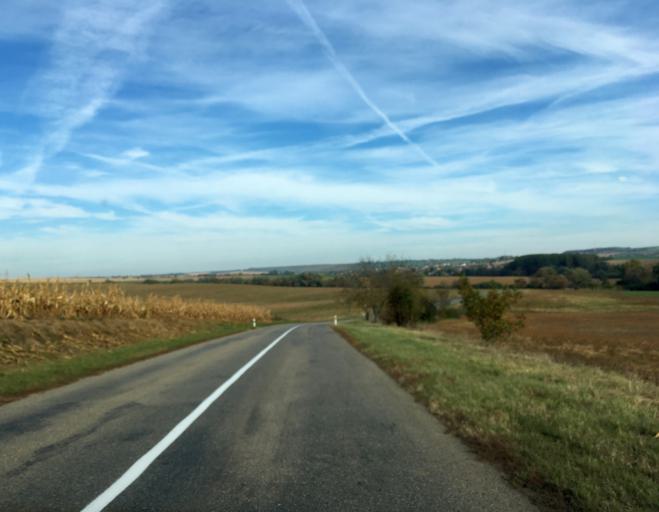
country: SK
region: Nitriansky
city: Svodin
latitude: 47.9965
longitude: 18.4083
